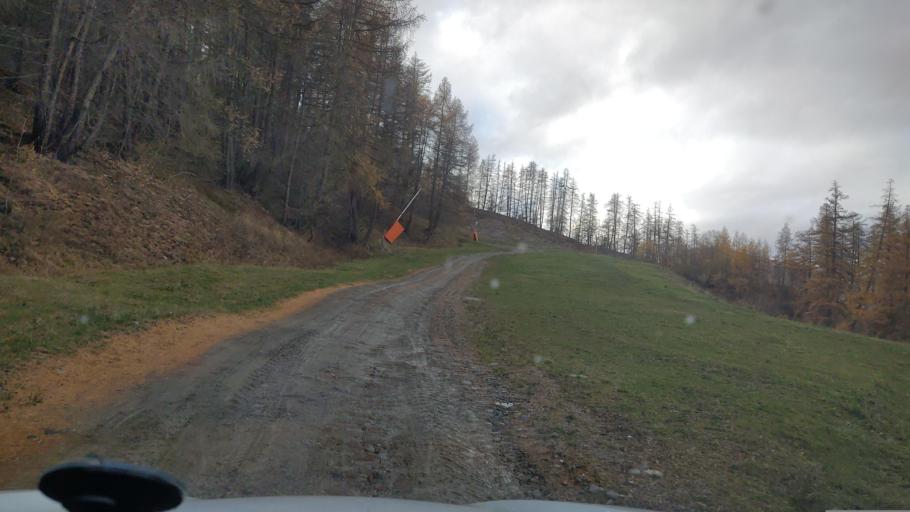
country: FR
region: Rhone-Alpes
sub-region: Departement de la Savoie
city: Valloire
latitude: 45.1526
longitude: 6.4393
